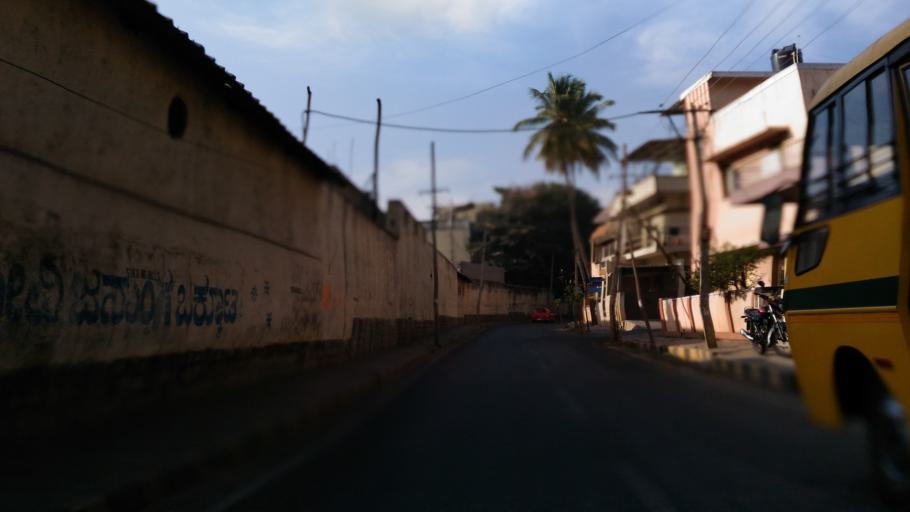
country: IN
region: Karnataka
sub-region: Bangalore Urban
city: Bangalore
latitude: 12.9417
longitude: 77.5651
